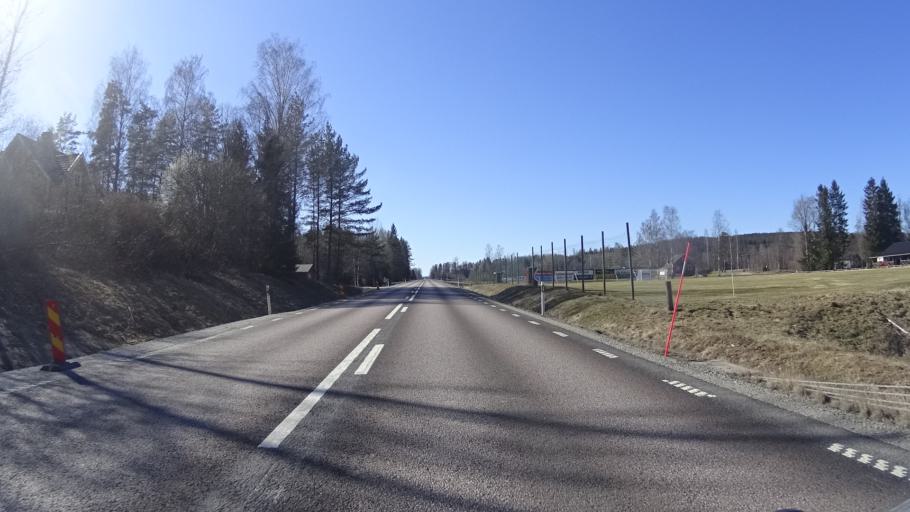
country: SE
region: Vaermland
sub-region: Arvika Kommun
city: Arvika
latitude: 59.6657
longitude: 12.8619
